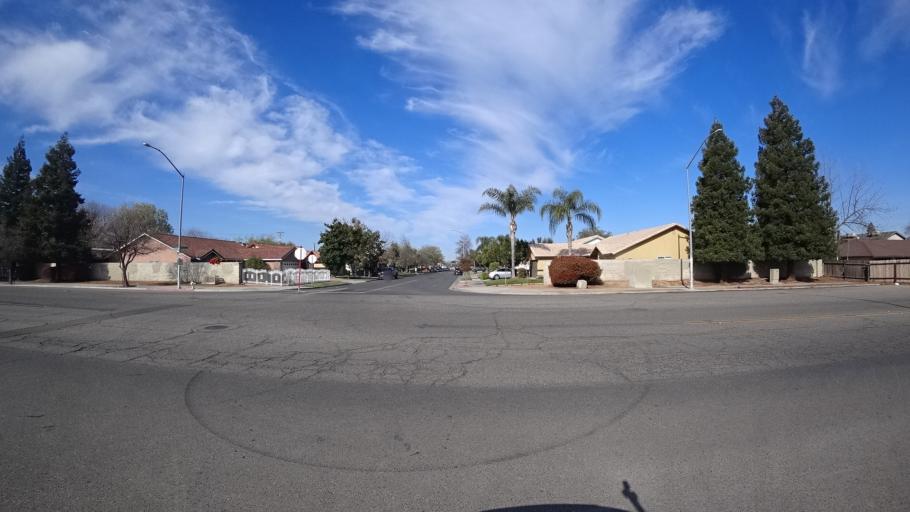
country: US
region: California
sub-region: Fresno County
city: West Park
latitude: 36.8041
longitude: -119.8894
